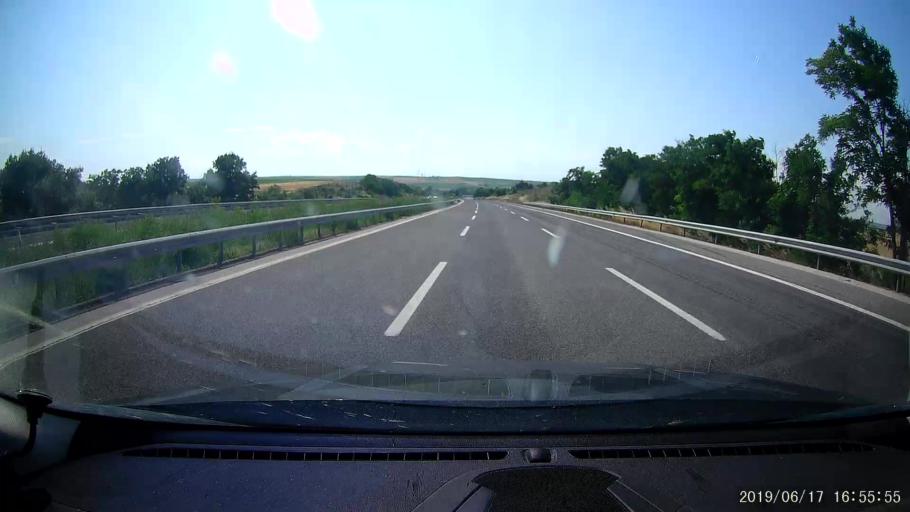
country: TR
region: Edirne
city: Haskoy
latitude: 41.5827
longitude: 26.9516
